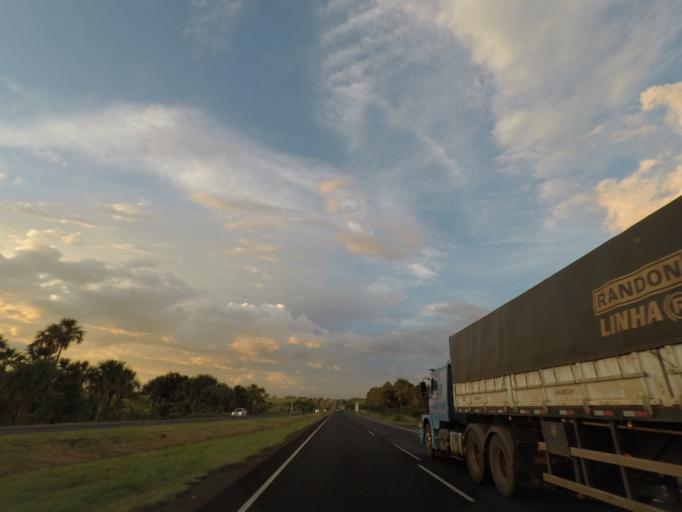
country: BR
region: Minas Gerais
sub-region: Uberaba
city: Uberaba
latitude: -19.6605
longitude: -48.0021
